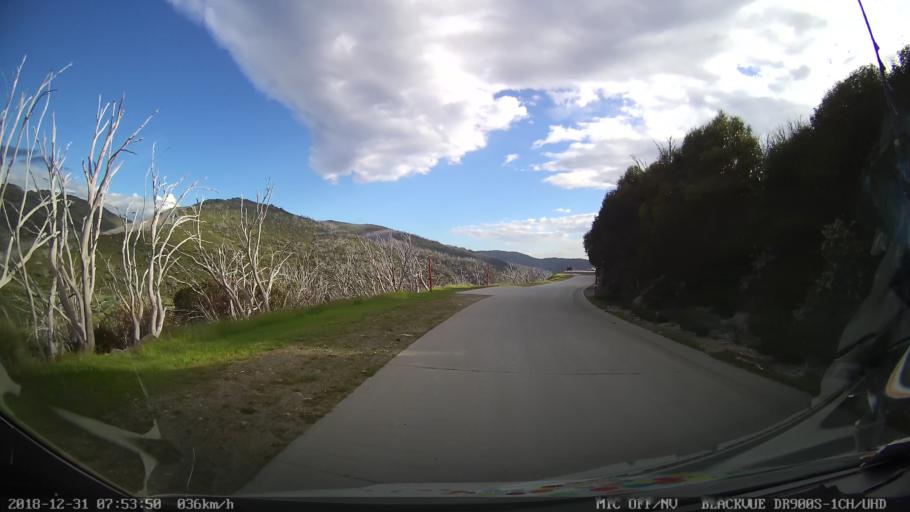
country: AU
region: New South Wales
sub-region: Snowy River
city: Jindabyne
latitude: -36.3791
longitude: 148.3744
